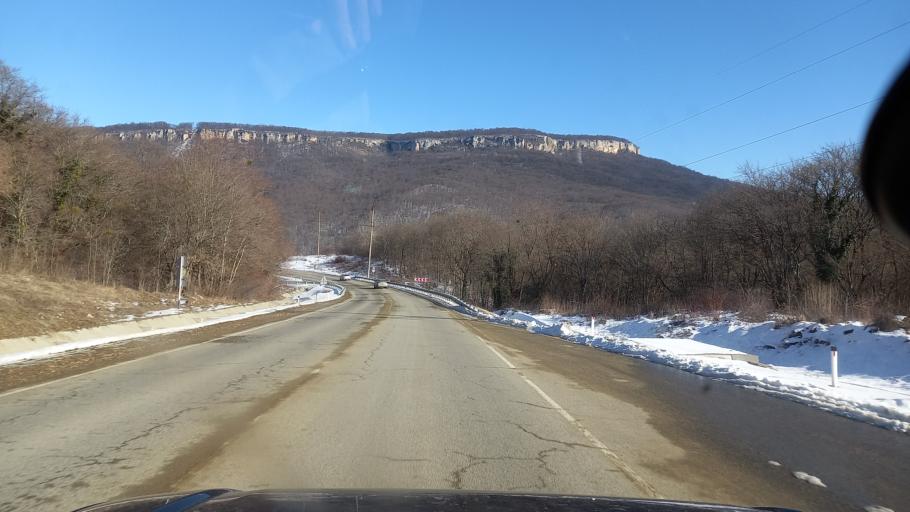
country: RU
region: Adygeya
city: Kamennomostskiy
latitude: 44.2408
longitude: 40.1910
